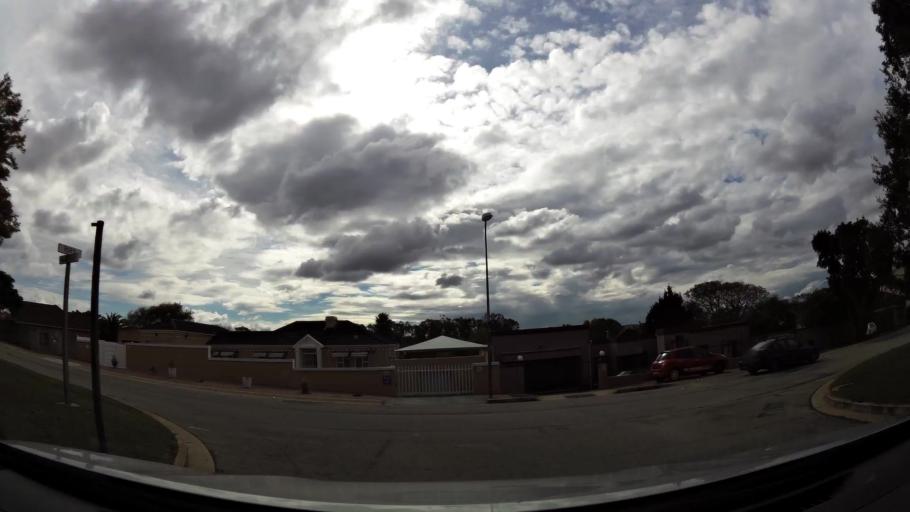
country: ZA
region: Eastern Cape
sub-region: Nelson Mandela Bay Metropolitan Municipality
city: Port Elizabeth
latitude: -33.9322
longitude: 25.5081
